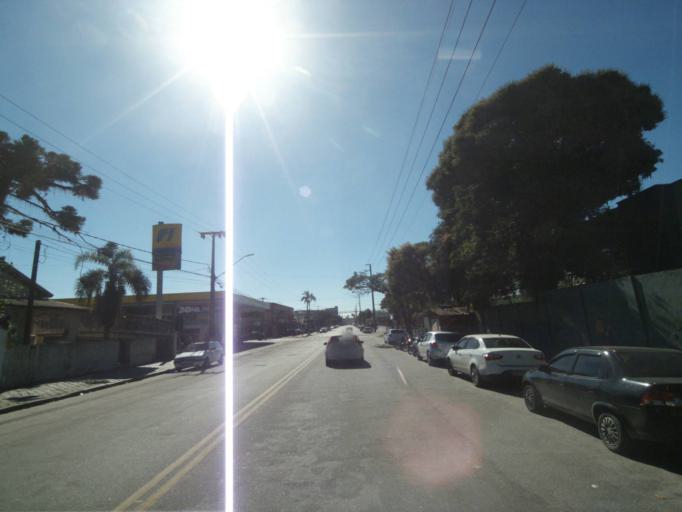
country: BR
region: Parana
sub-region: Paranagua
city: Paranagua
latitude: -25.5156
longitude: -48.5145
